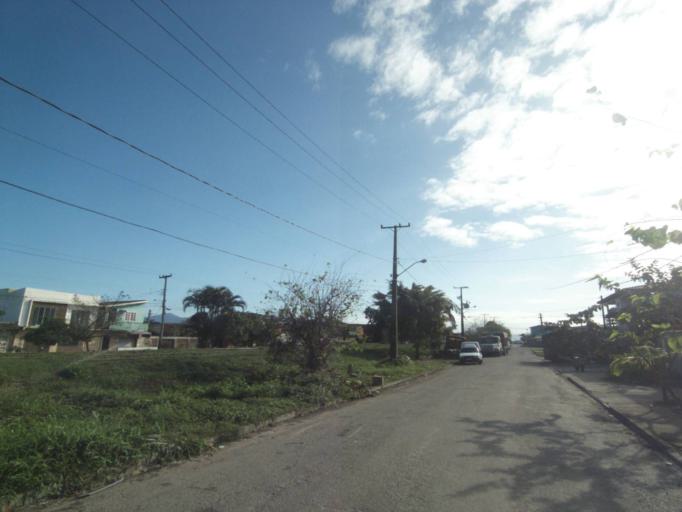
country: BR
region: Parana
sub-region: Paranagua
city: Paranagua
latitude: -25.5266
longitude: -48.5294
